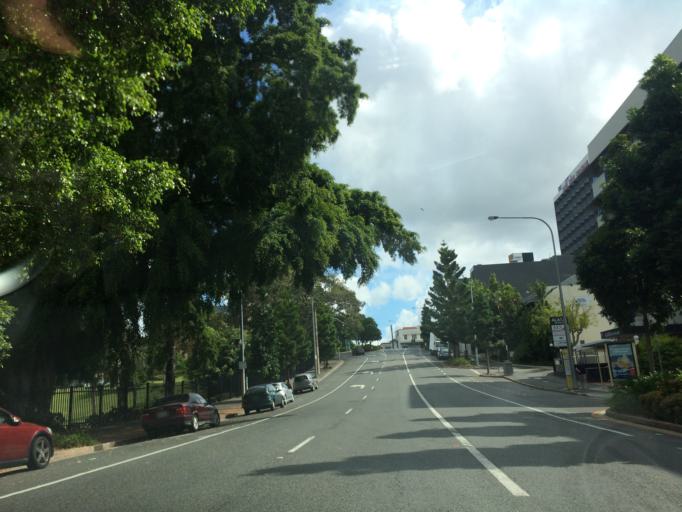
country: AU
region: Queensland
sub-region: Brisbane
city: Spring Hill
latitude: -27.4636
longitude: 153.0208
